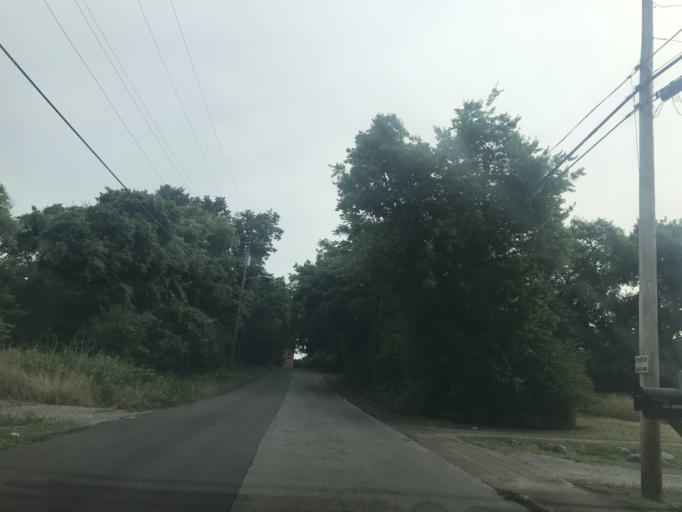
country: US
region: Tennessee
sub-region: Davidson County
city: Nashville
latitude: 36.1940
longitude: -86.8274
